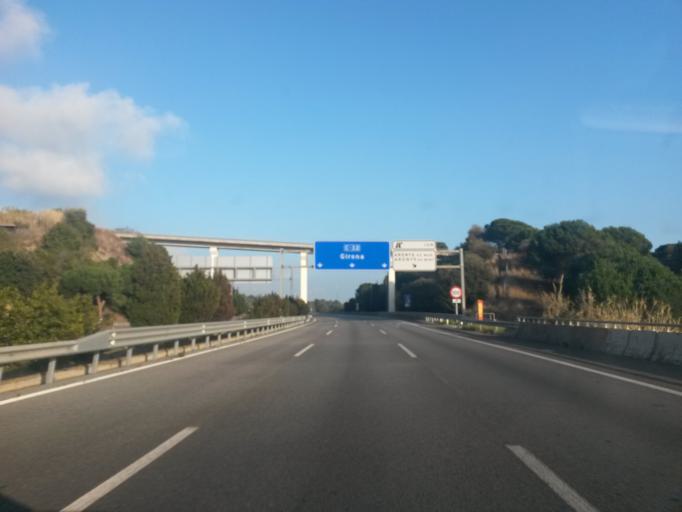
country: ES
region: Catalonia
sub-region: Provincia de Barcelona
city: Caldes d'Estrac
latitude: 41.5777
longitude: 2.5249
